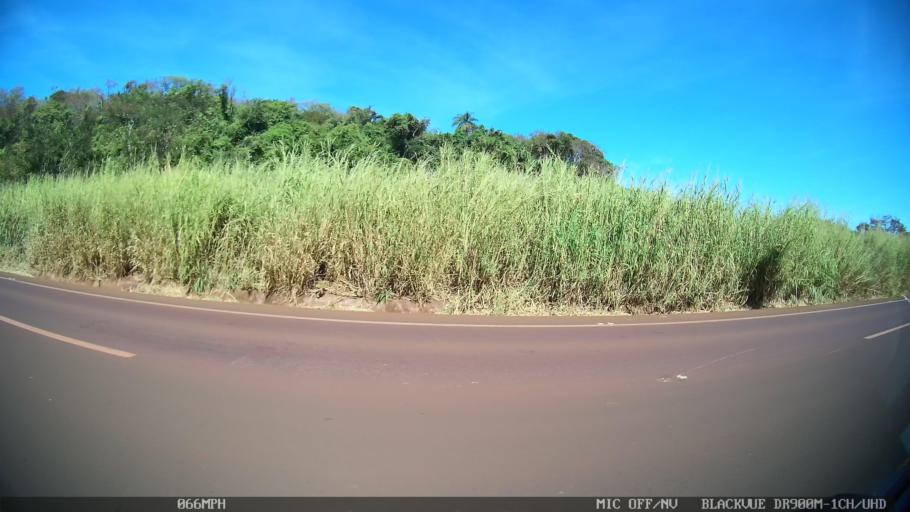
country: BR
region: Sao Paulo
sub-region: Sao Joaquim Da Barra
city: Sao Joaquim da Barra
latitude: -20.5503
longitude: -47.6512
